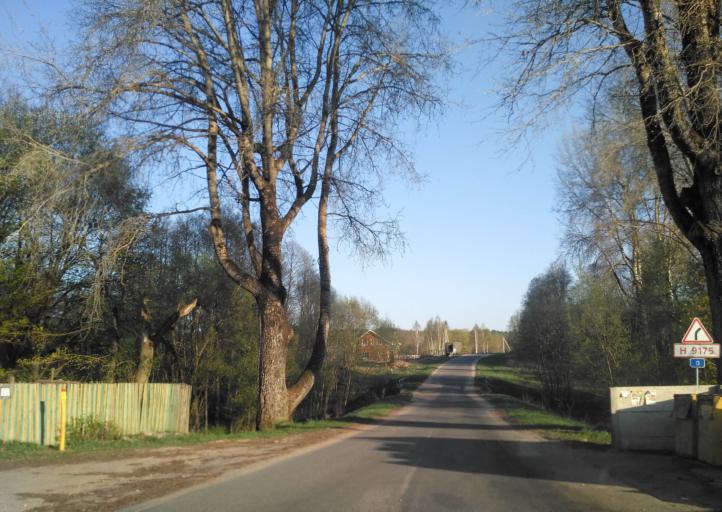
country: BY
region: Minsk
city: Pyatryshki
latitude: 54.1104
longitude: 27.1903
